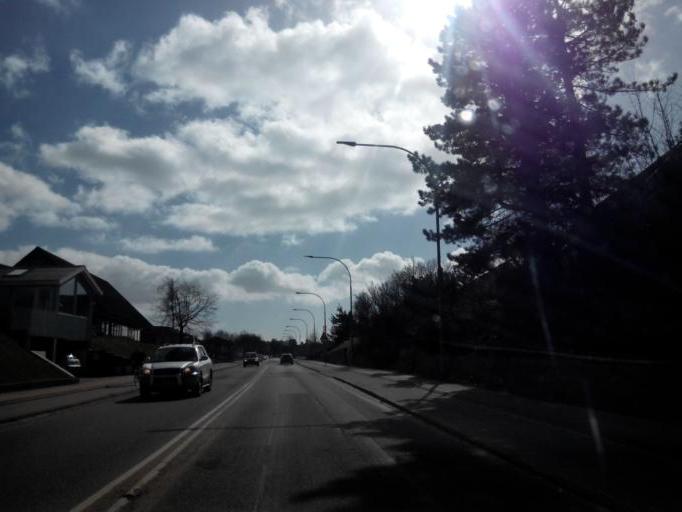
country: DK
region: Central Jutland
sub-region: Syddjurs Kommune
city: Ebeltoft
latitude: 56.1986
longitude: 10.6812
